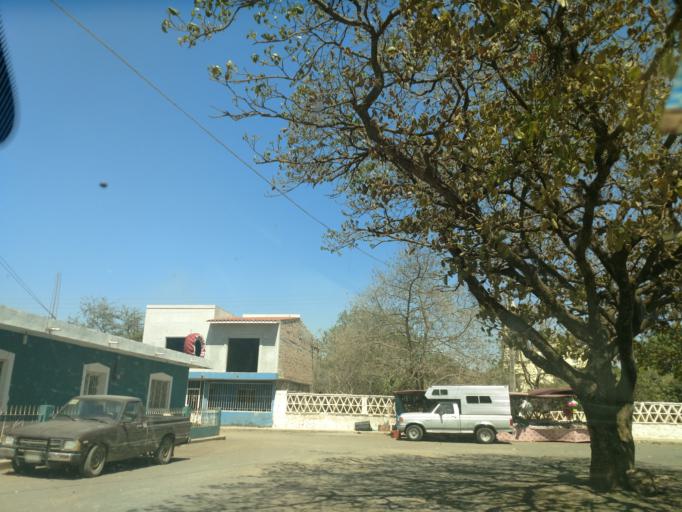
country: MX
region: Nayarit
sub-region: Tepic
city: La Corregidora
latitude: 21.5010
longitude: -104.7035
